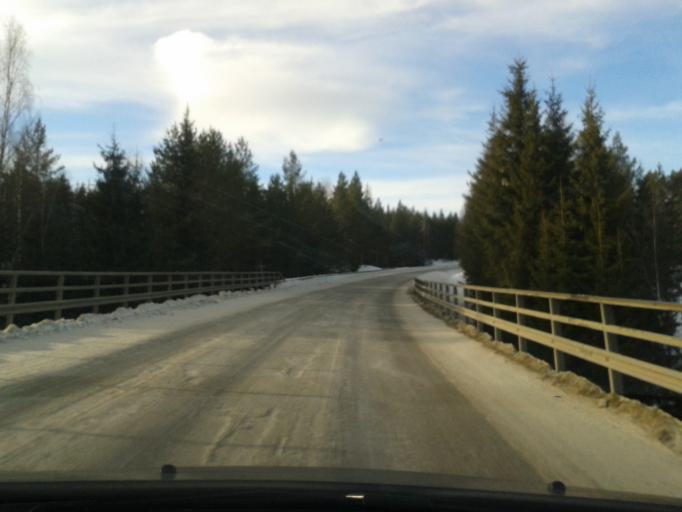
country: SE
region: Vaesternorrland
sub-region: OErnskoeldsviks Kommun
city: Bredbyn
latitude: 63.5307
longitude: 17.9722
